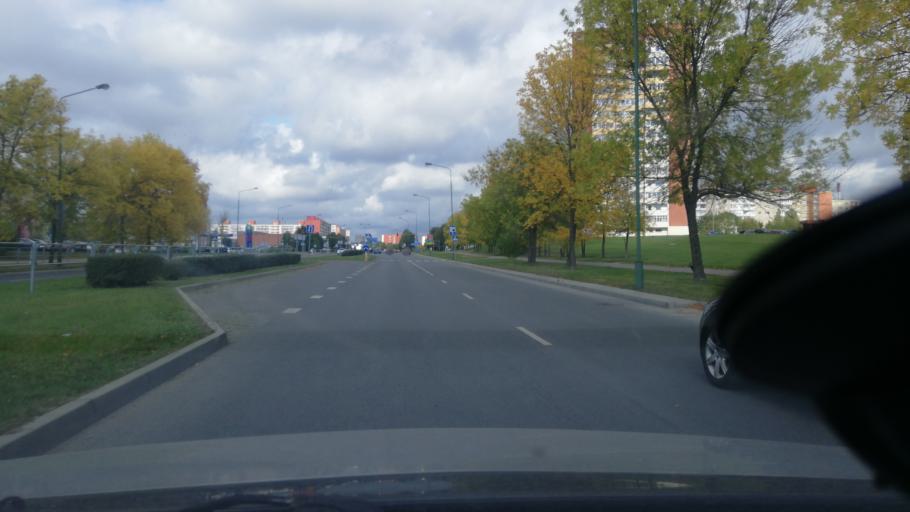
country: LT
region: Klaipedos apskritis
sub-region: Klaipeda
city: Klaipeda
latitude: 55.6685
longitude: 21.1947
